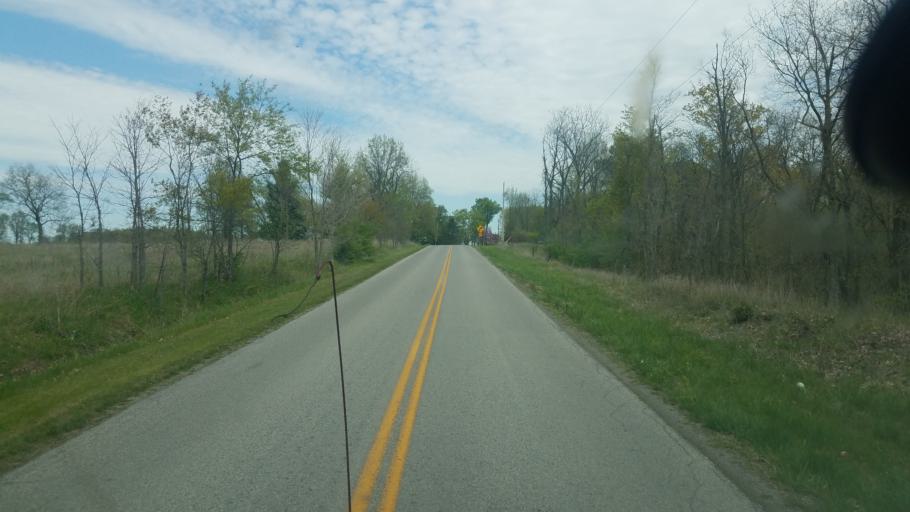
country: US
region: Ohio
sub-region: Allen County
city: Lima
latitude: 40.7811
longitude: -83.9790
